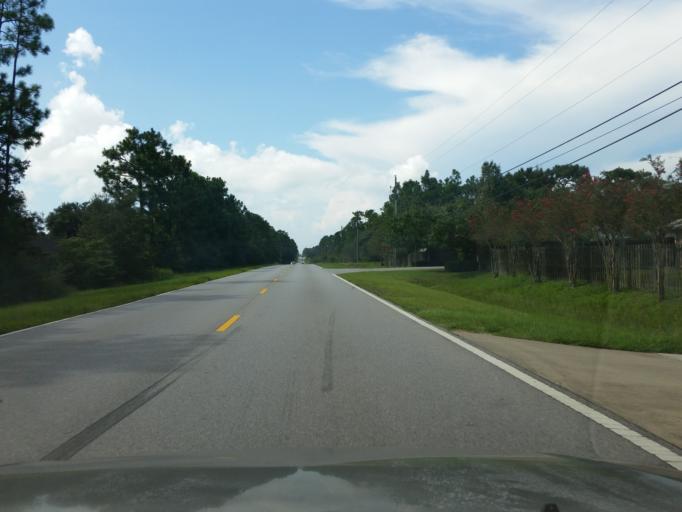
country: US
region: Florida
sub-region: Escambia County
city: Myrtle Grove
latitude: 30.3582
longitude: -87.4028
